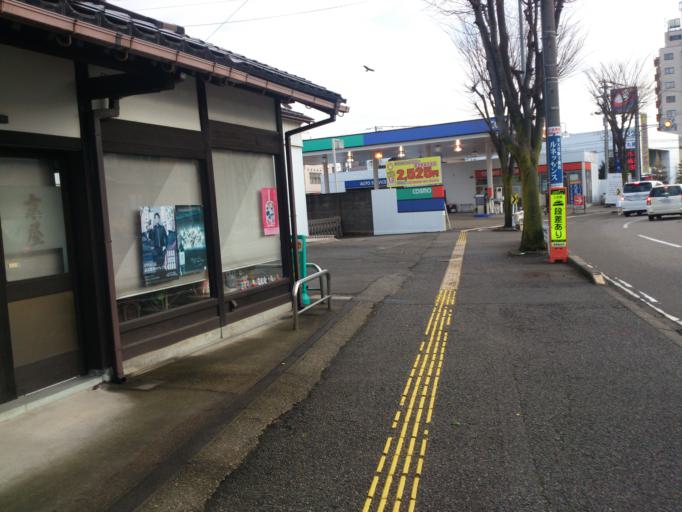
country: JP
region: Ishikawa
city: Kanazawa-shi
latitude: 36.5806
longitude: 136.6562
